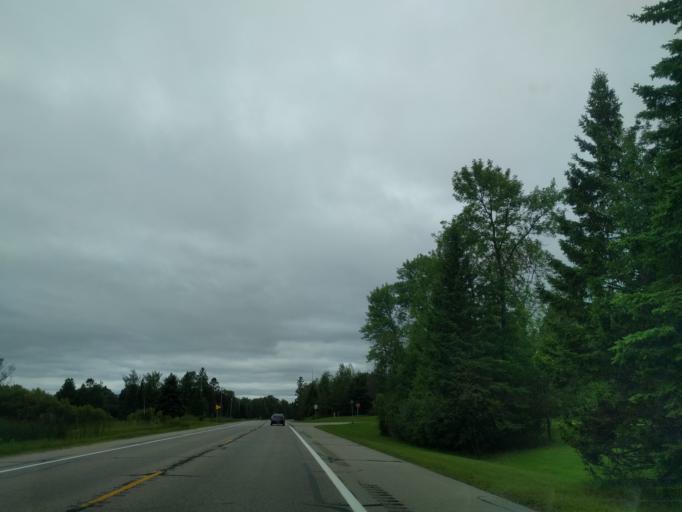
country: US
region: Michigan
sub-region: Delta County
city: Escanaba
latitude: 45.6731
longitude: -87.1504
